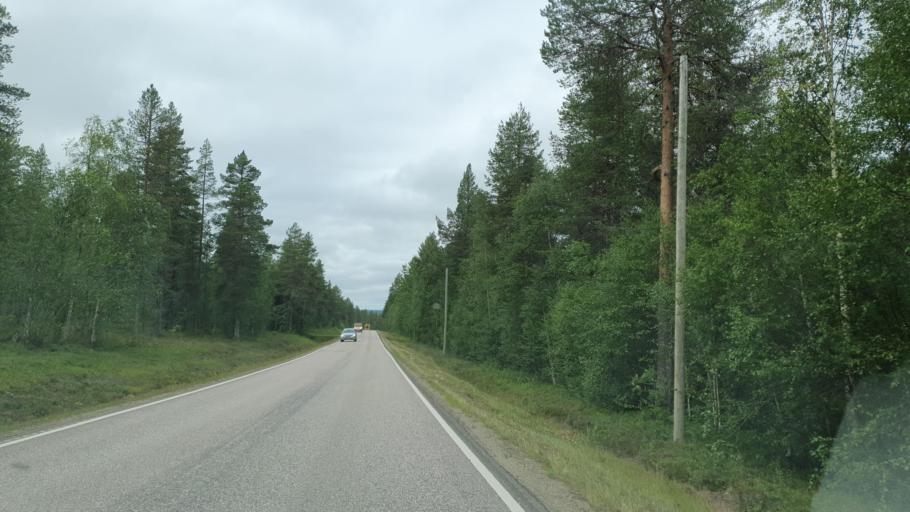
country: FI
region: Lapland
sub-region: Pohjois-Lappi
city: Sodankylae
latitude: 67.4171
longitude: 26.2761
